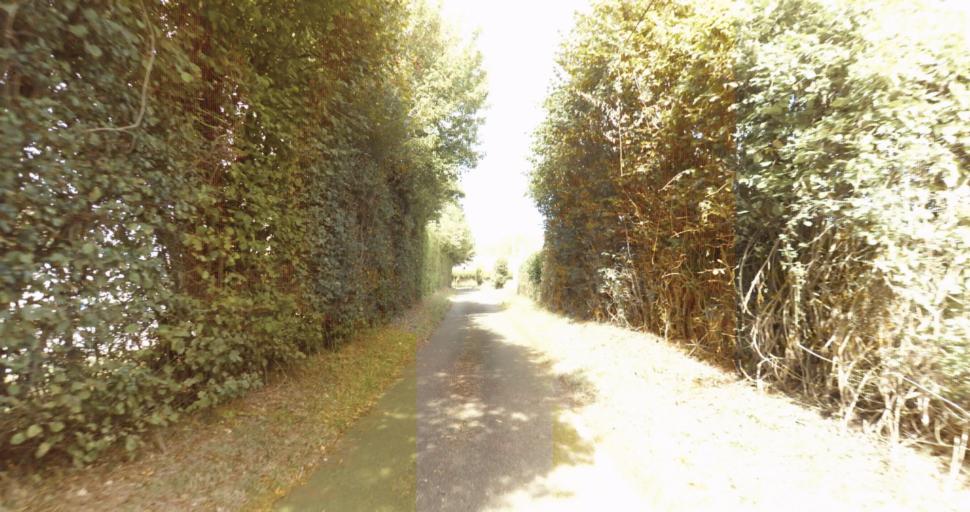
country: FR
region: Lower Normandy
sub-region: Departement de l'Orne
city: Sees
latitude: 48.7015
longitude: 0.2117
